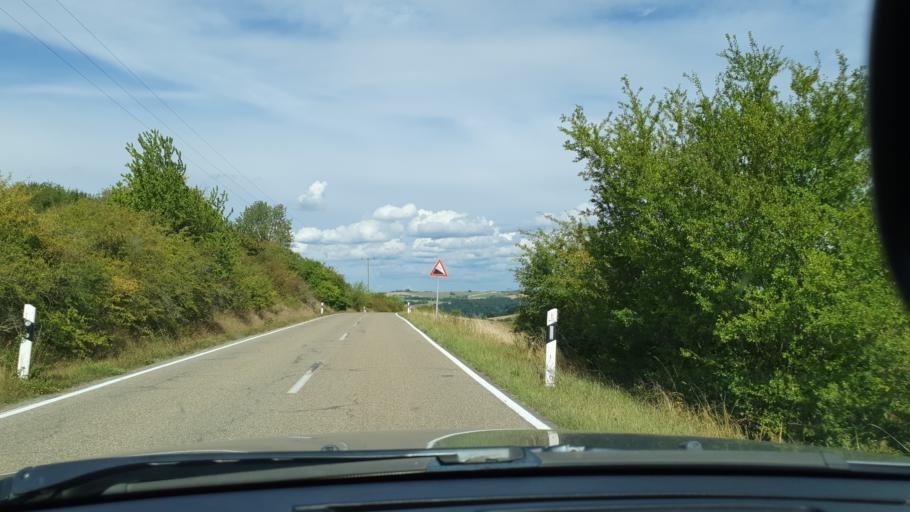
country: DE
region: Rheinland-Pfalz
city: Contwig
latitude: 49.2364
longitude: 7.4067
